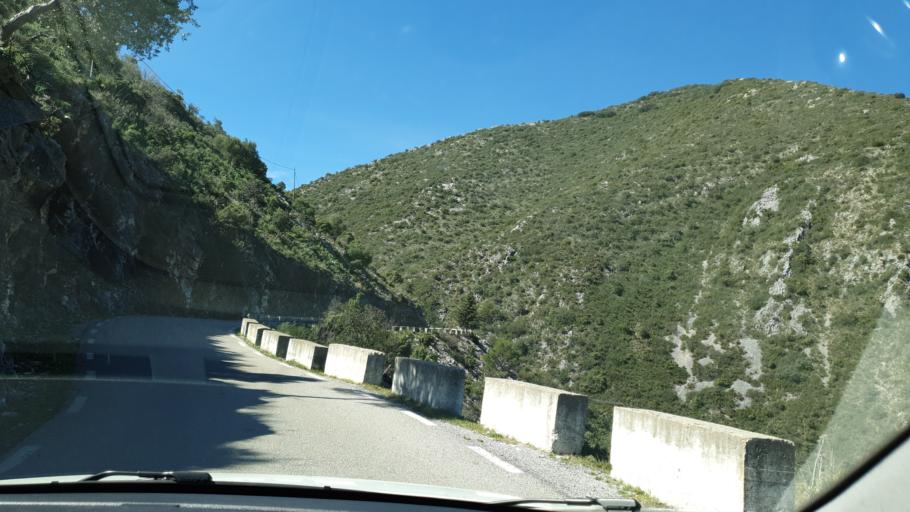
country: ES
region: Andalusia
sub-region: Provincia de Malaga
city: Ojen
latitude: 36.5896
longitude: -4.8783
